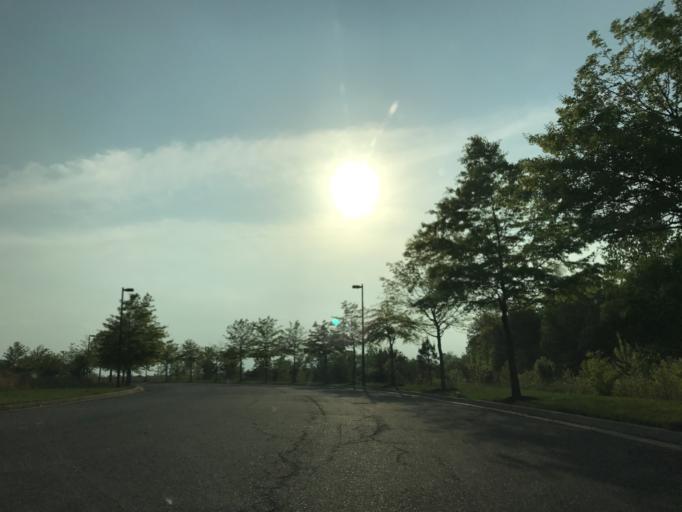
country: US
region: Maryland
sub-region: Baltimore County
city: White Marsh
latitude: 39.3758
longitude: -76.4422
